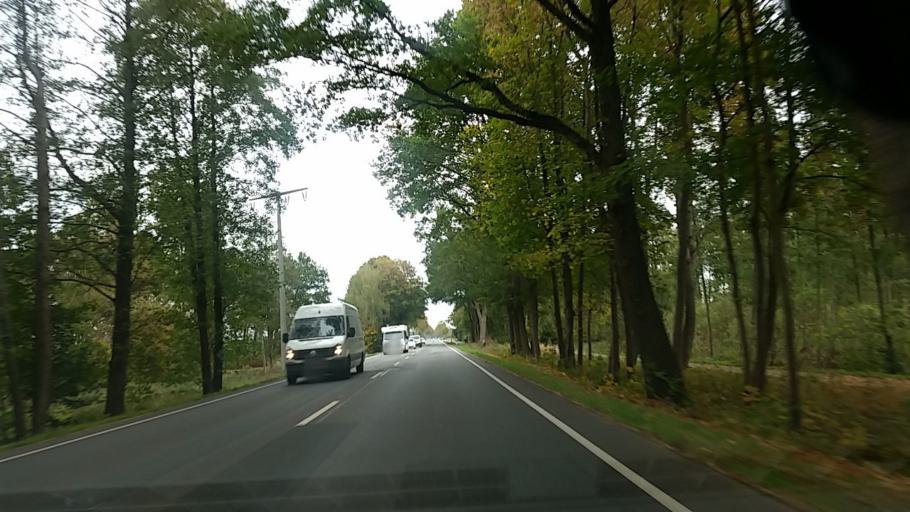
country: DE
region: Lower Saxony
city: Gross Oesingen
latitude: 52.6581
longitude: 10.4649
